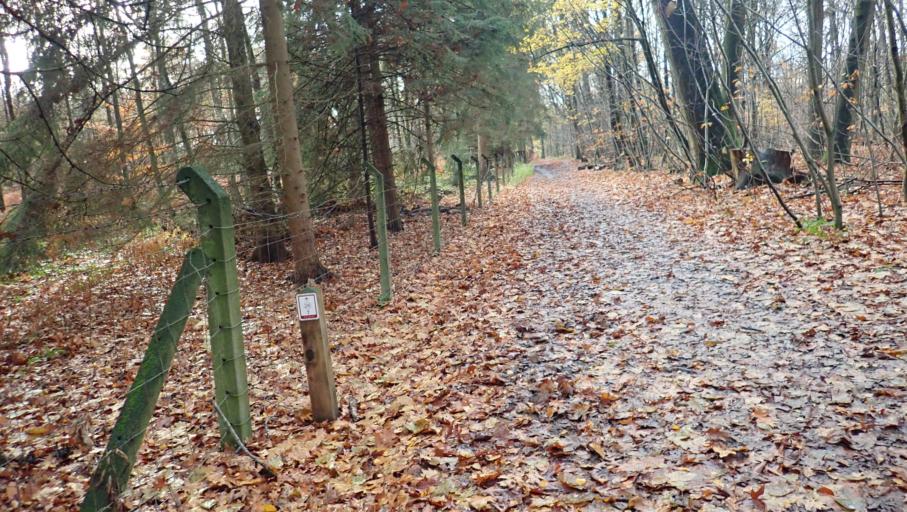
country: BE
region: Flanders
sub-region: Provincie Vlaams-Brabant
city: Opwijk
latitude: 50.9316
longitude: 4.1615
